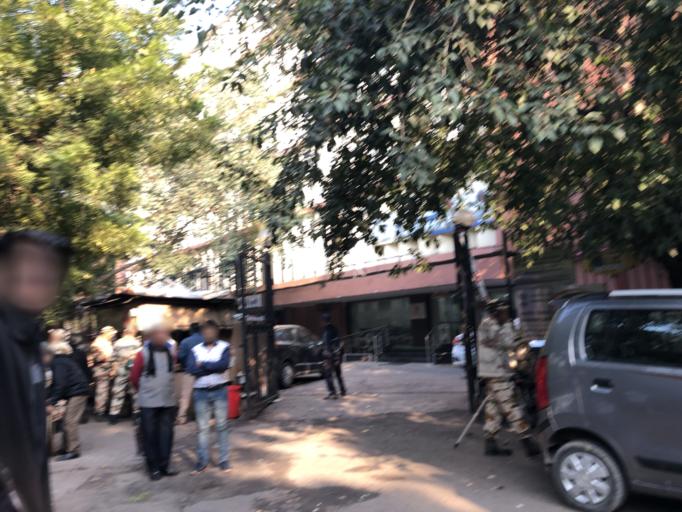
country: IN
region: NCT
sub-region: New Delhi
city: New Delhi
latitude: 28.6247
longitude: 77.2139
